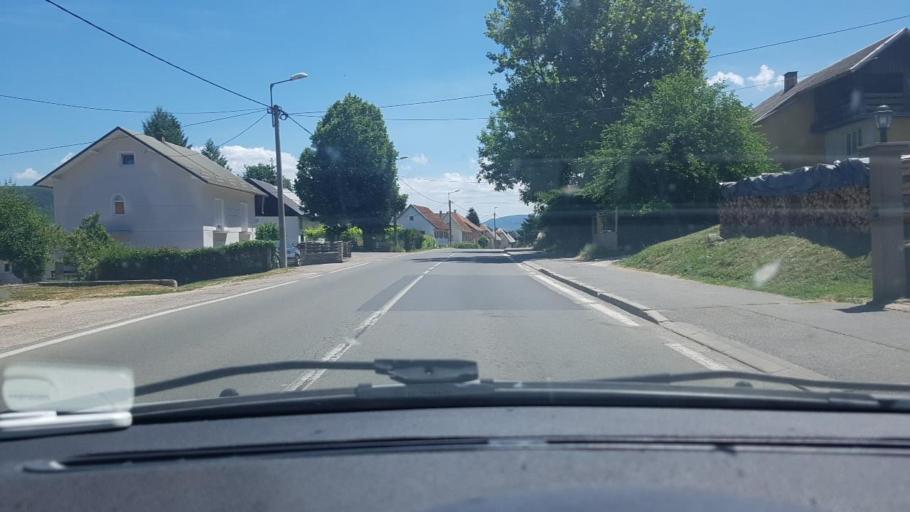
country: HR
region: Licko-Senjska
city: Otocac
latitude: 44.8685
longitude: 15.2466
